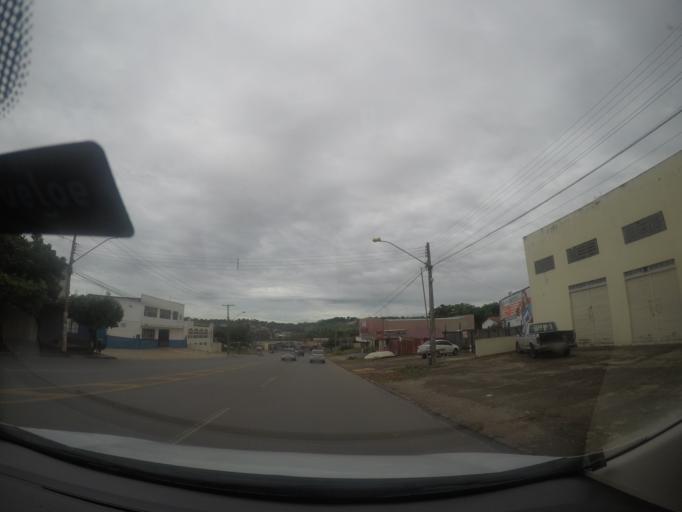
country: BR
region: Goias
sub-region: Goiania
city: Goiania
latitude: -16.6295
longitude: -49.2852
